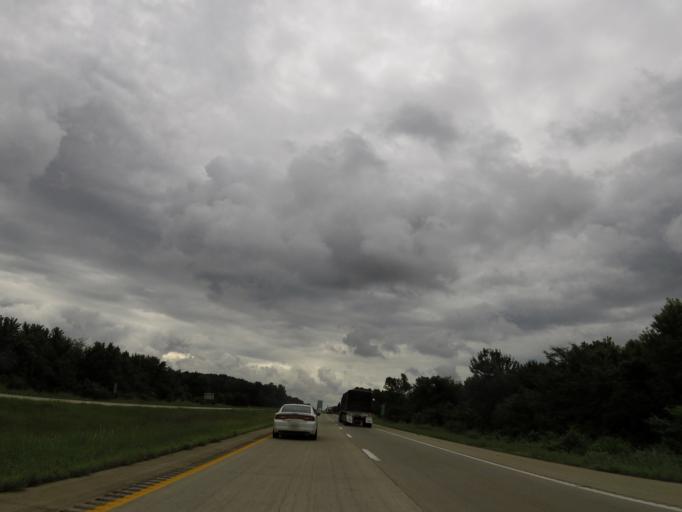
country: US
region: Illinois
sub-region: Alexander County
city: Cairo
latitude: 37.0052
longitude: -89.2251
